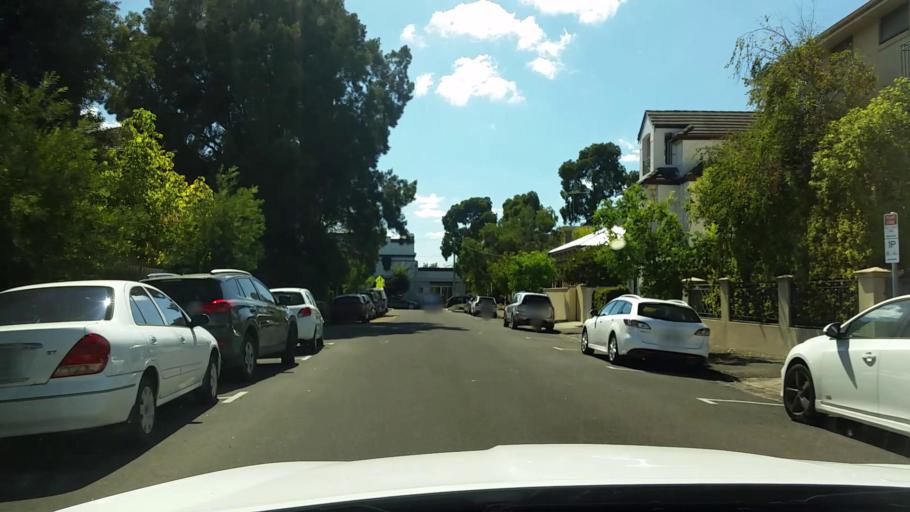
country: AU
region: Victoria
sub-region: Stonnington
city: Windsor
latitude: -37.8579
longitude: 144.9892
